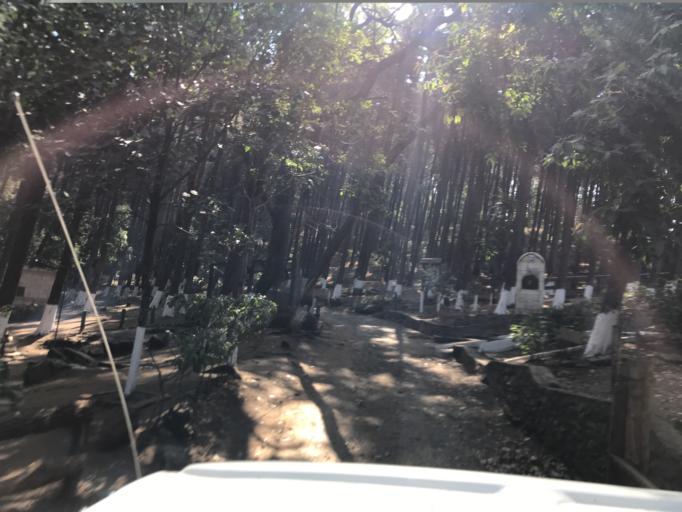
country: GT
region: Guatemala
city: Petapa
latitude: 14.4834
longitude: -90.5569
